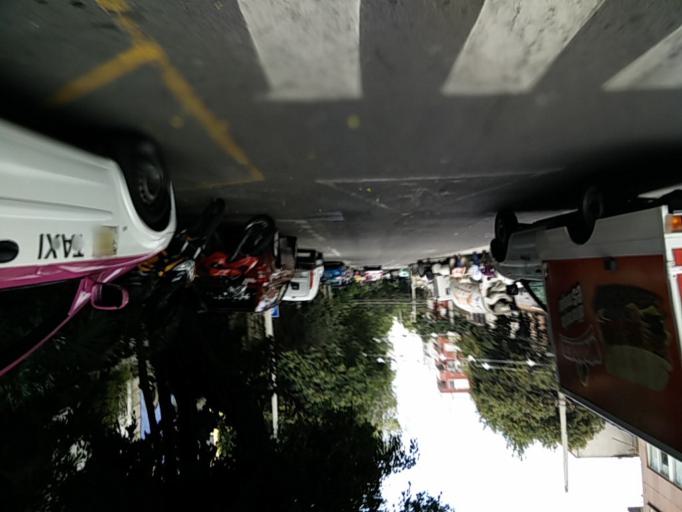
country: MX
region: Mexico City
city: Benito Juarez
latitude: 19.4189
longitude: -99.1613
